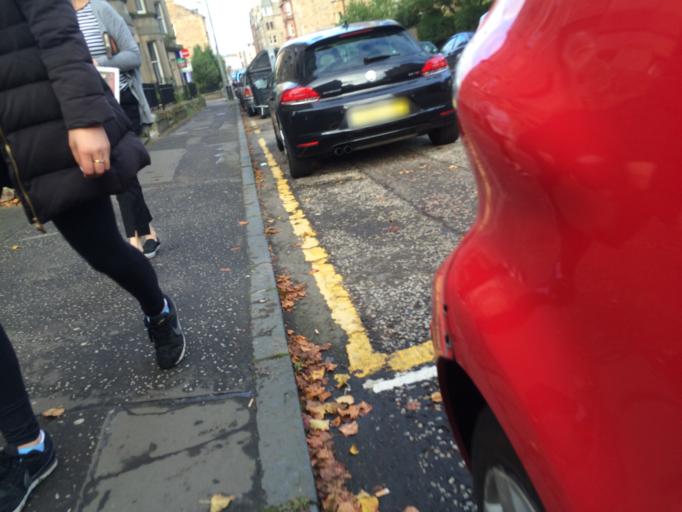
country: GB
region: Scotland
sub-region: Edinburgh
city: Edinburgh
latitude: 55.9387
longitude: -3.2106
